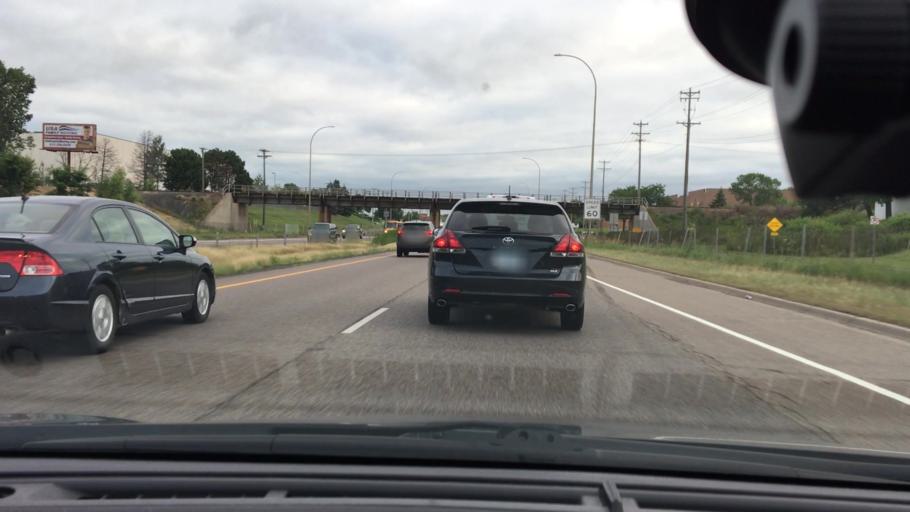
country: US
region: Minnesota
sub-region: Hennepin County
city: New Hope
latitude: 45.0478
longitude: -93.4008
